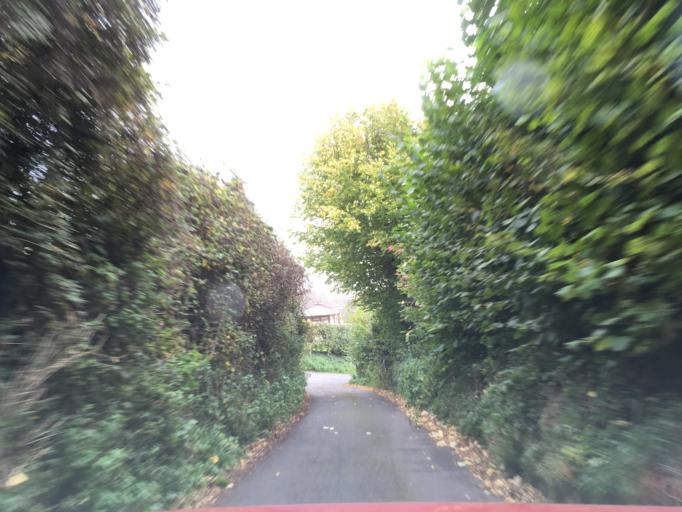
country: GB
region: England
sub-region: Gloucestershire
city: Stonehouse
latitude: 51.7518
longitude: -2.2550
